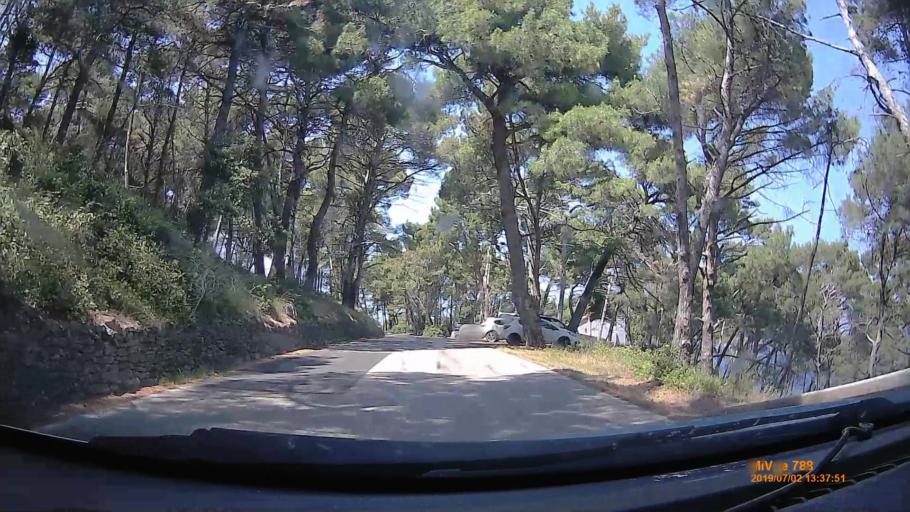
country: HR
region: Primorsko-Goranska
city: Mali Losinj
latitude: 44.5259
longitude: 14.4890
